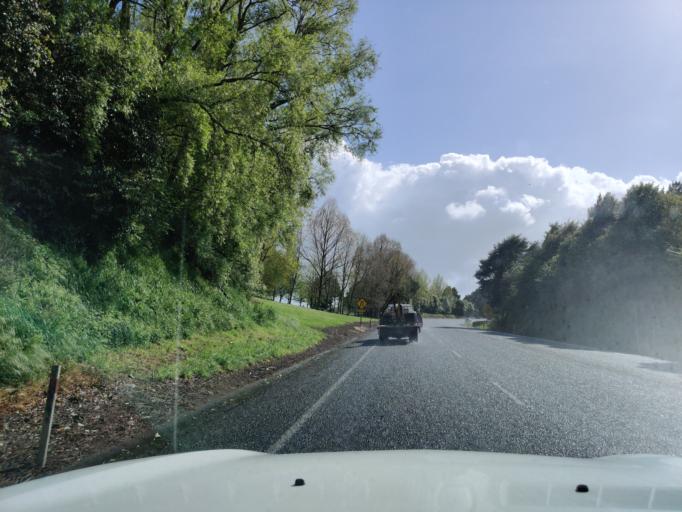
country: NZ
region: Waikato
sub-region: Matamata-Piako District
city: Matamata
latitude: -37.9454
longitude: 175.6573
